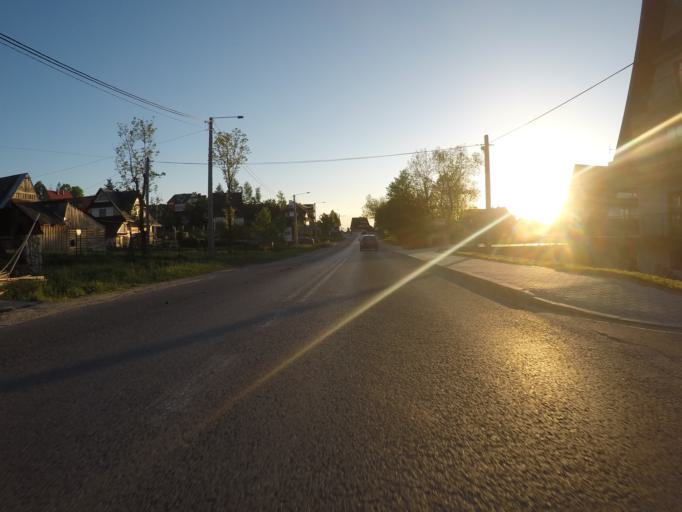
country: PL
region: Lesser Poland Voivodeship
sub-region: Powiat tatrzanski
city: Poronin
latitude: 49.2894
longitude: 20.0175
